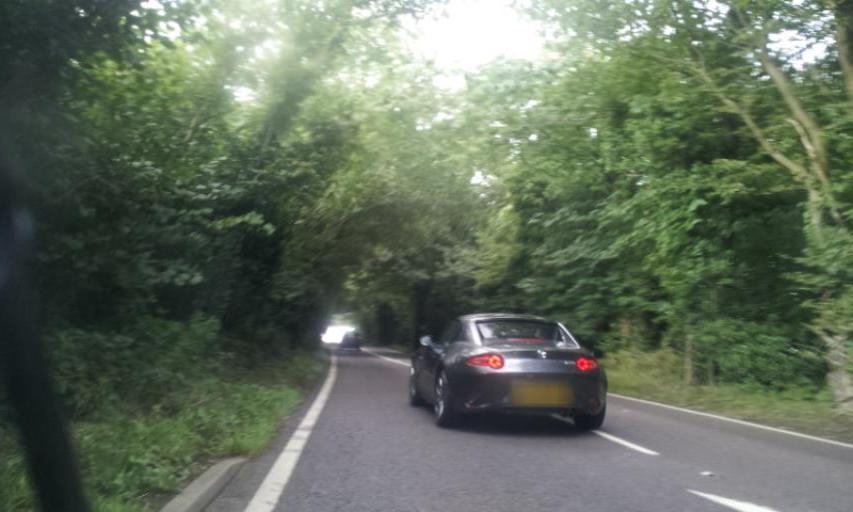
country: GB
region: England
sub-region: Kent
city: Kings Hill
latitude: 51.2648
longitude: 0.3618
